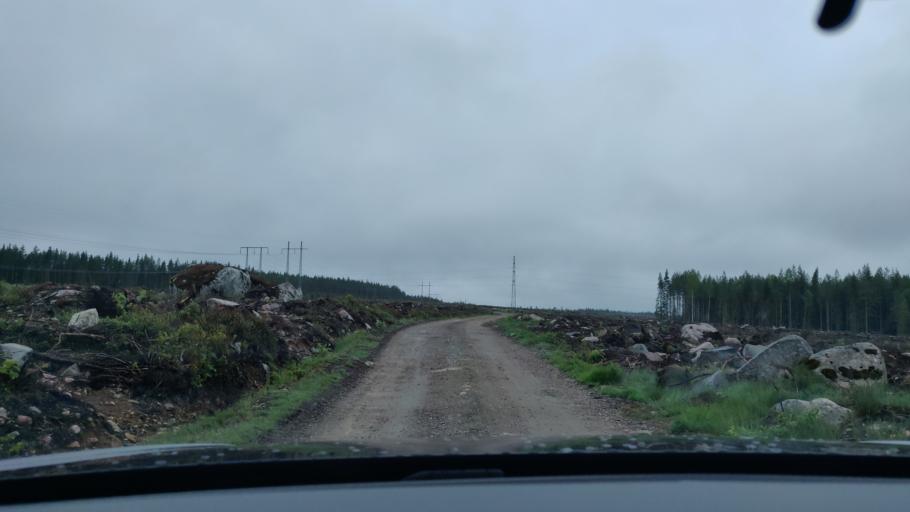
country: SE
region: Dalarna
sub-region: Avesta Kommun
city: Horndal
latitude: 60.3093
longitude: 16.4016
